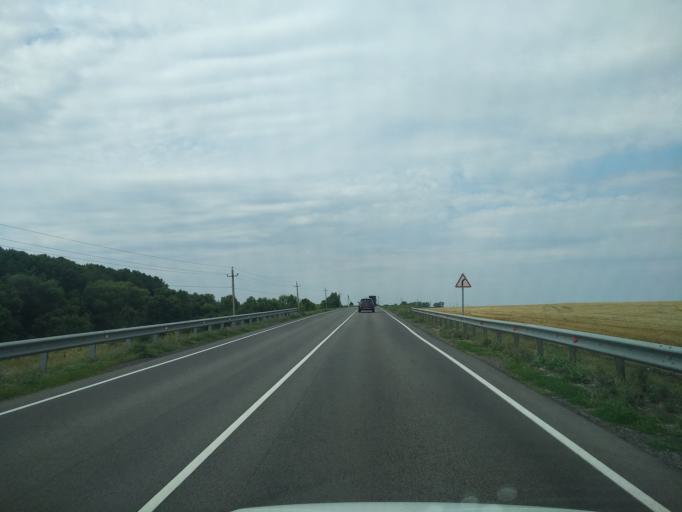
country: RU
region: Voronezj
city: Pereleshinskiy
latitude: 51.8172
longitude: 40.2619
